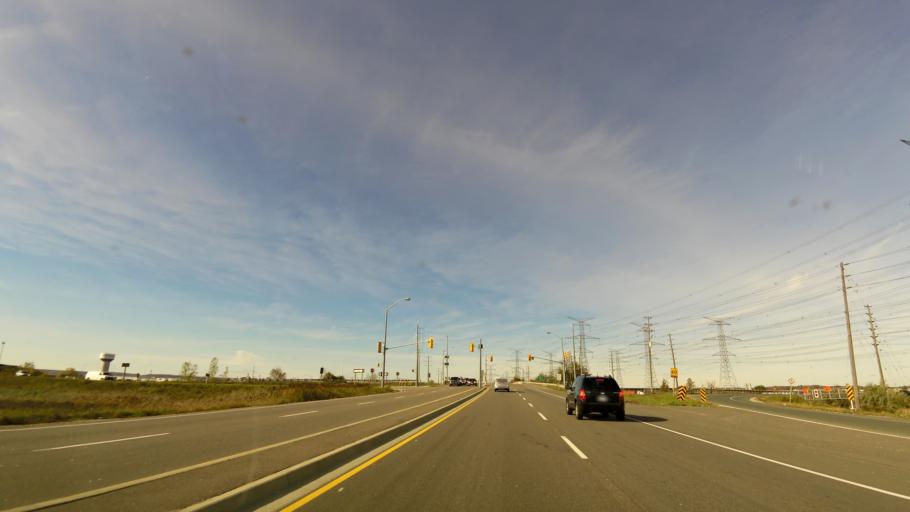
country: CA
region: Ontario
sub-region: Halton
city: Milton
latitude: 43.5405
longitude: -79.8602
